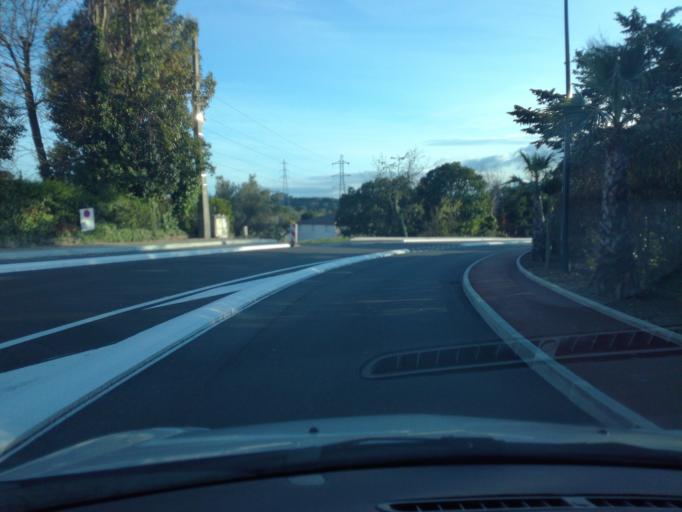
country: FR
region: Provence-Alpes-Cote d'Azur
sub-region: Departement des Alpes-Maritimes
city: Mougins
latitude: 43.6059
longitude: 7.0120
